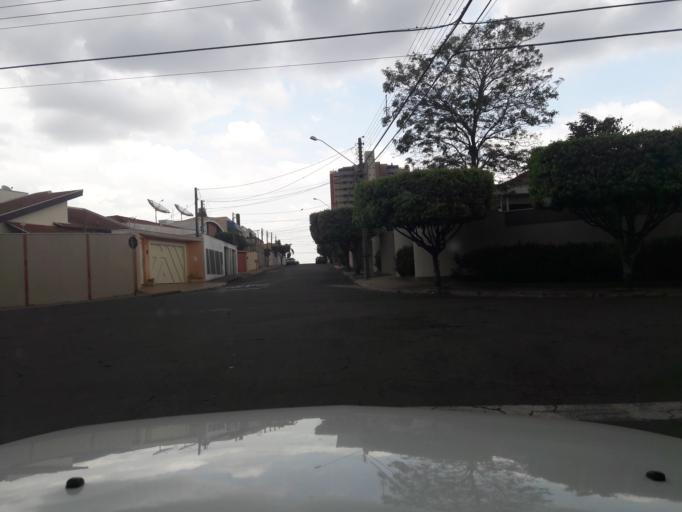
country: BR
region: Sao Paulo
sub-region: Moji-Guacu
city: Mogi-Gaucu
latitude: -22.3666
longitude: -46.9371
